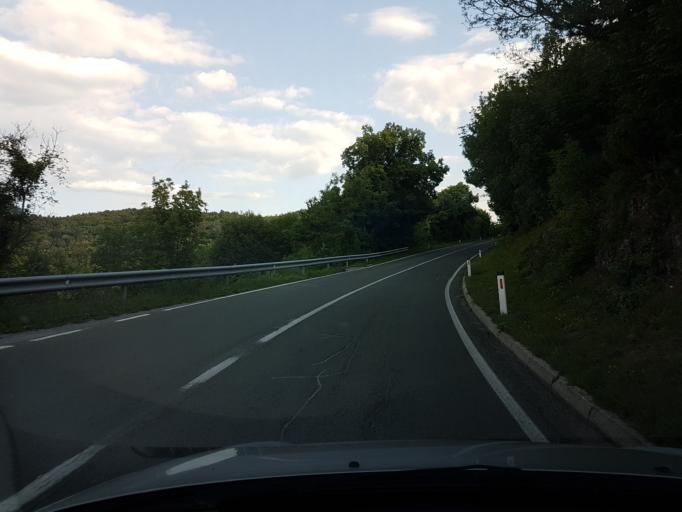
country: SI
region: Sezana
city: Sezana
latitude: 45.7061
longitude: 13.9001
